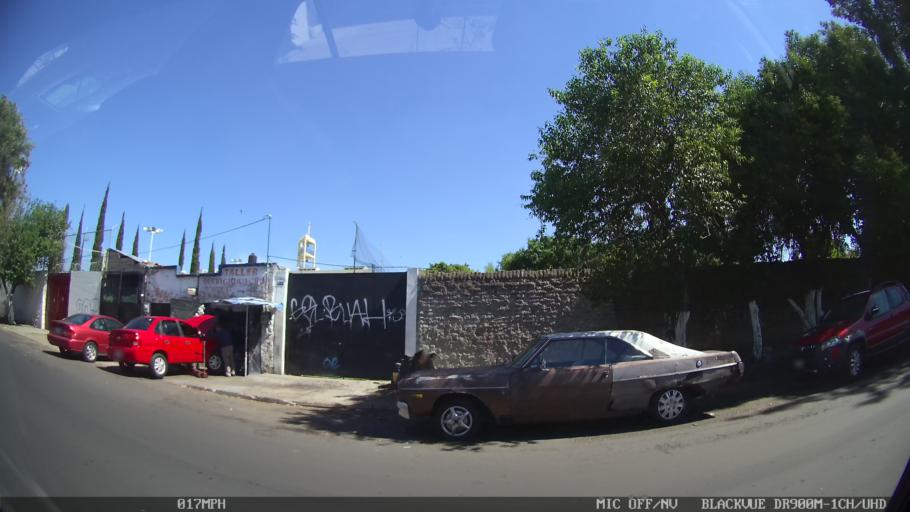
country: MX
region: Jalisco
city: Tlaquepaque
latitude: 20.6514
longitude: -103.2899
